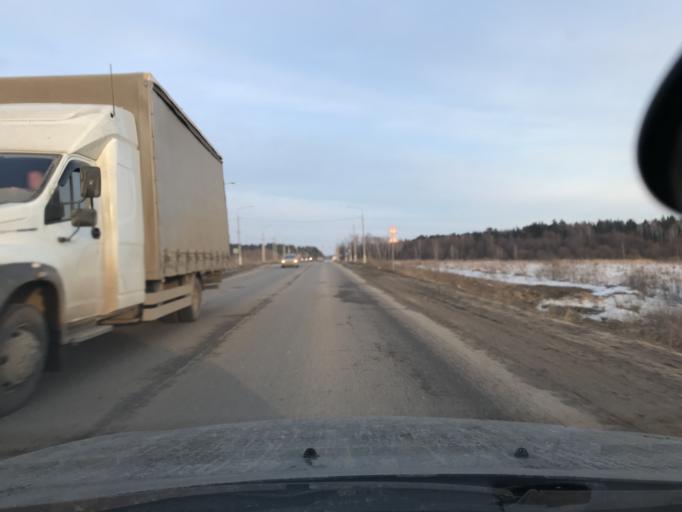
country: RU
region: Kaluga
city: Kaluga
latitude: 54.4658
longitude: 36.2514
